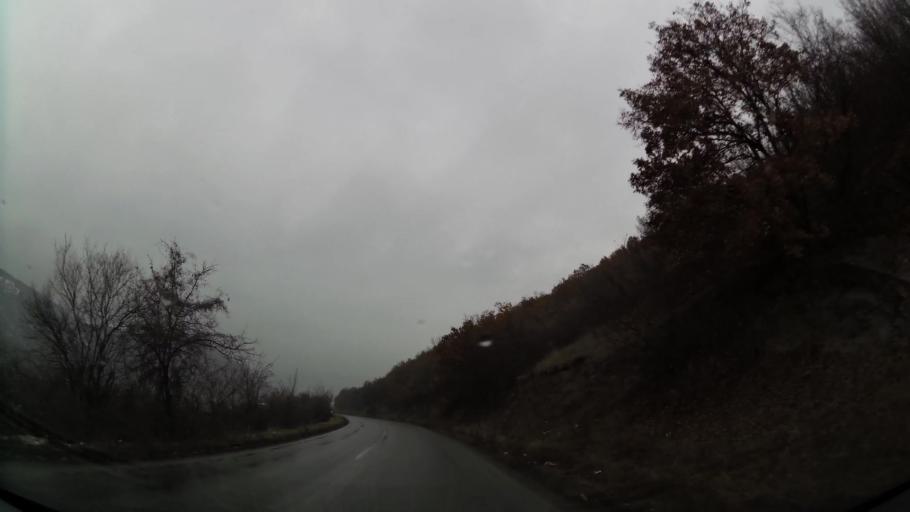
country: XK
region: Ferizaj
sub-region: Hani i Elezit
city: Hani i Elezit
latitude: 42.1325
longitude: 21.3116
